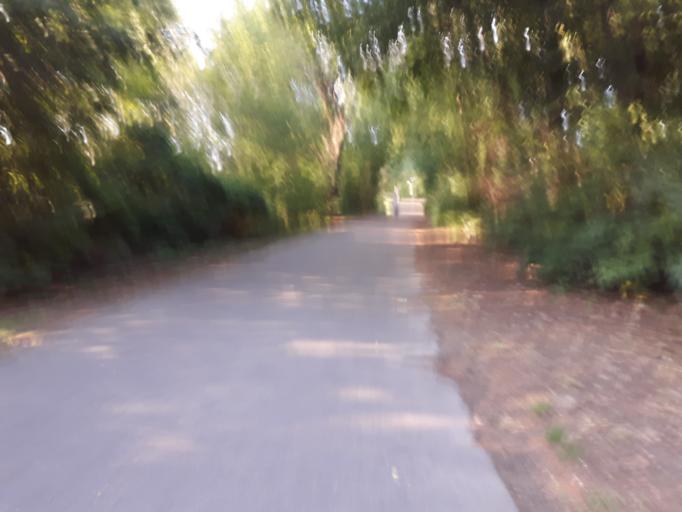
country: DE
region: Berlin
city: Staaken
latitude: 52.5533
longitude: 13.1460
